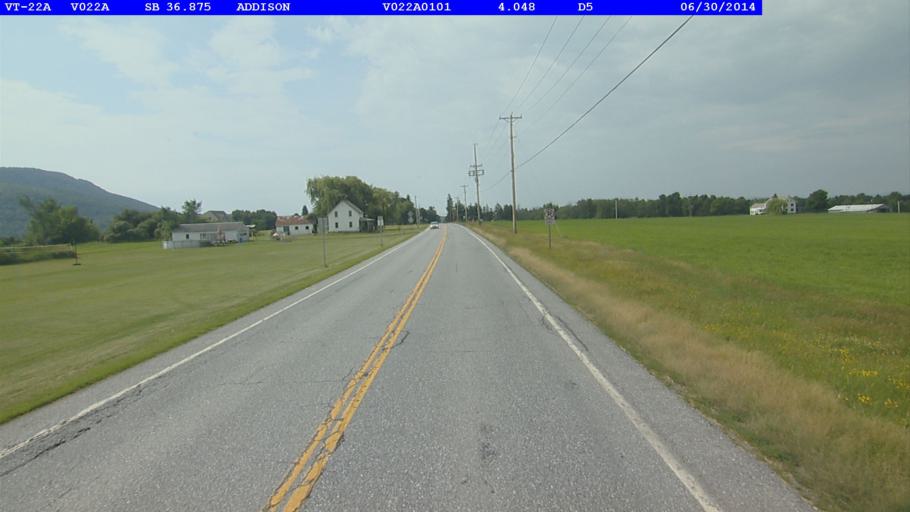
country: US
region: Vermont
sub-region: Addison County
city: Vergennes
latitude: 44.0878
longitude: -73.3025
